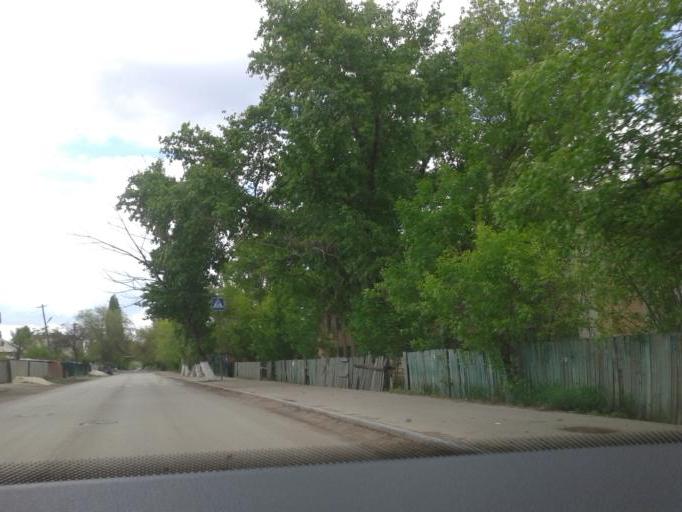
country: RU
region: Volgograd
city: Krasnoslobodsk
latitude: 48.5171
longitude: 44.5186
